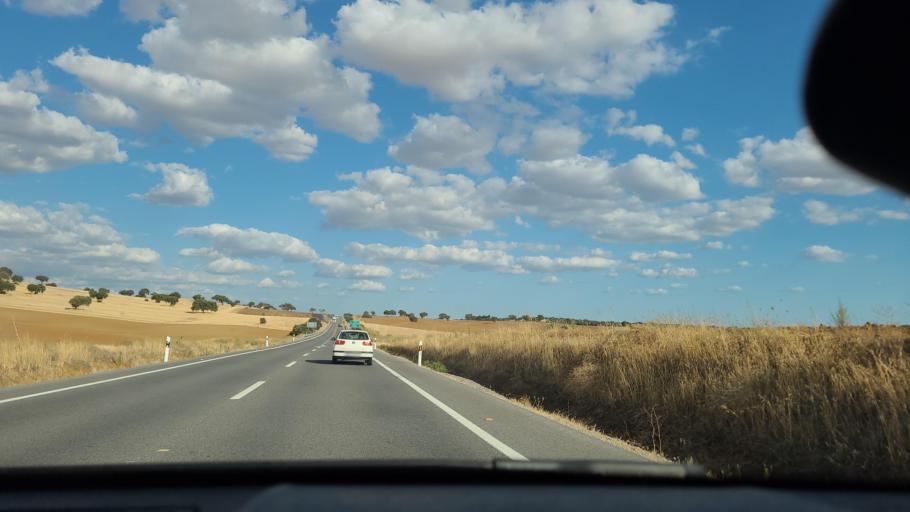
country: ES
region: Extremadura
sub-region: Provincia de Badajoz
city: Granja de Torrehermosa
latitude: 38.2957
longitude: -5.5478
